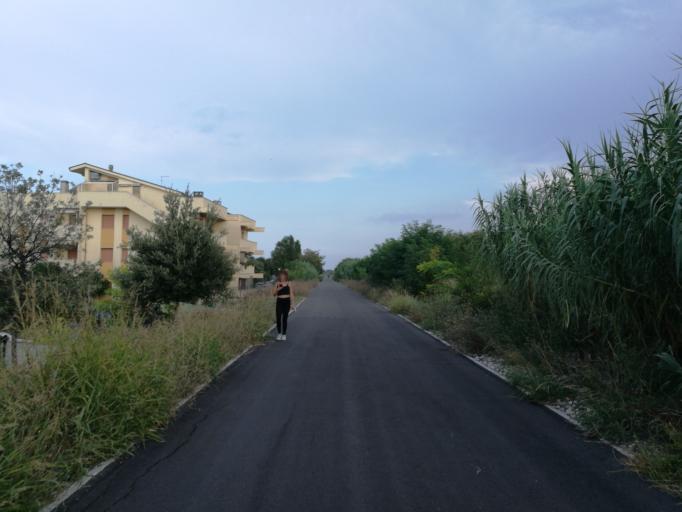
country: IT
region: Abruzzo
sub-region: Provincia di Chieti
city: Fossacesia
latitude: 42.2449
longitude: 14.5187
